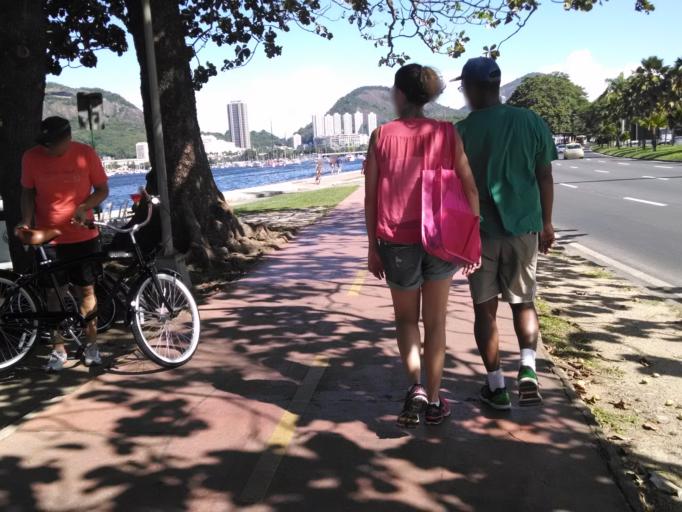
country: BR
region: Rio de Janeiro
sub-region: Rio De Janeiro
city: Rio de Janeiro
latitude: -22.9410
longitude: -43.1704
